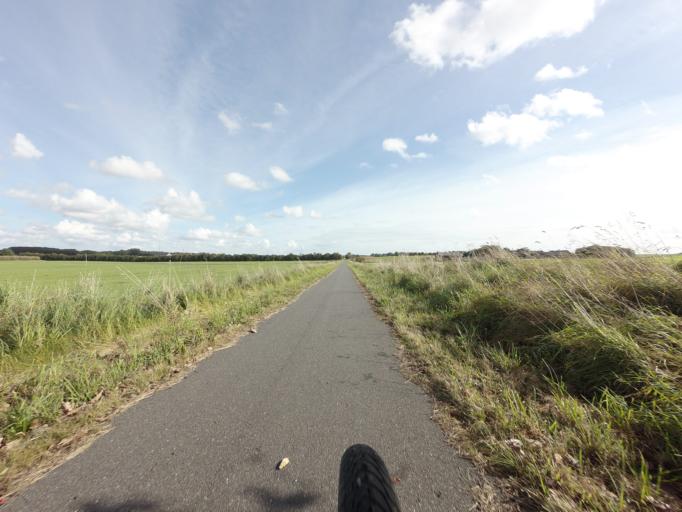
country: DK
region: Central Jutland
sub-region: Favrskov Kommune
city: Ulstrup
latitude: 56.5004
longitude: 9.7297
